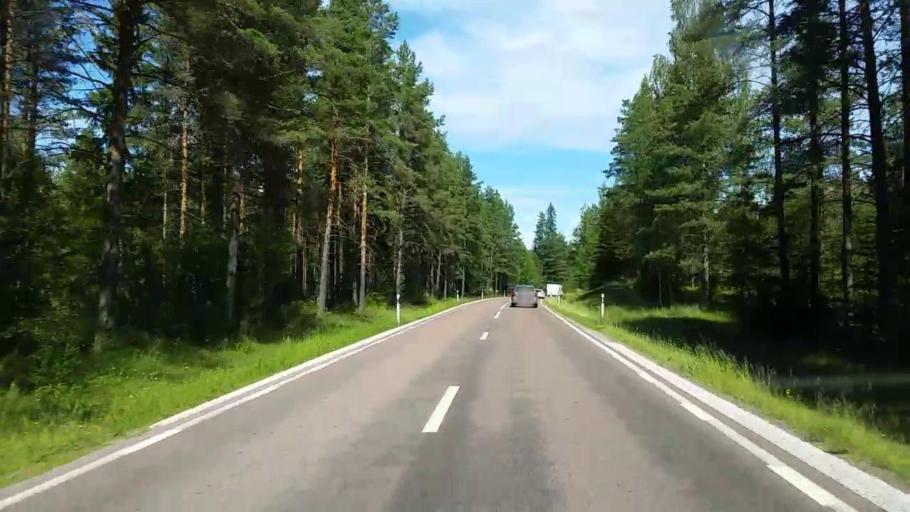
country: SE
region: Dalarna
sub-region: Rattviks Kommun
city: Raettvik
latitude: 60.9152
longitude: 15.2028
